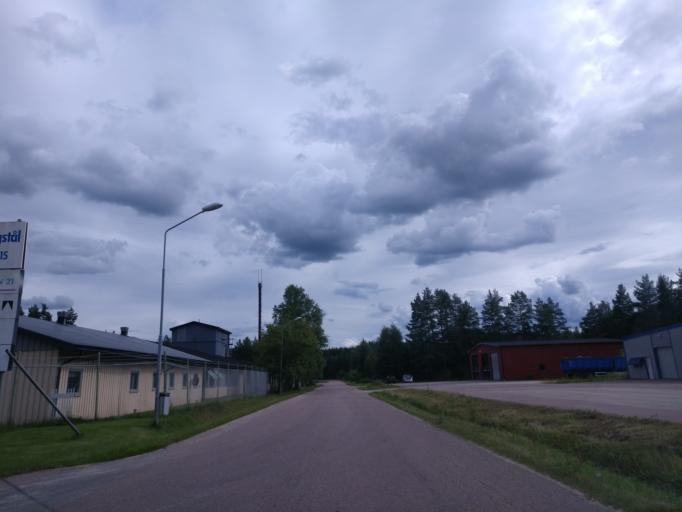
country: SE
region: Vaermland
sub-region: Hagfors Kommun
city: Ekshaerad
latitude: 60.1660
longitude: 13.4971
